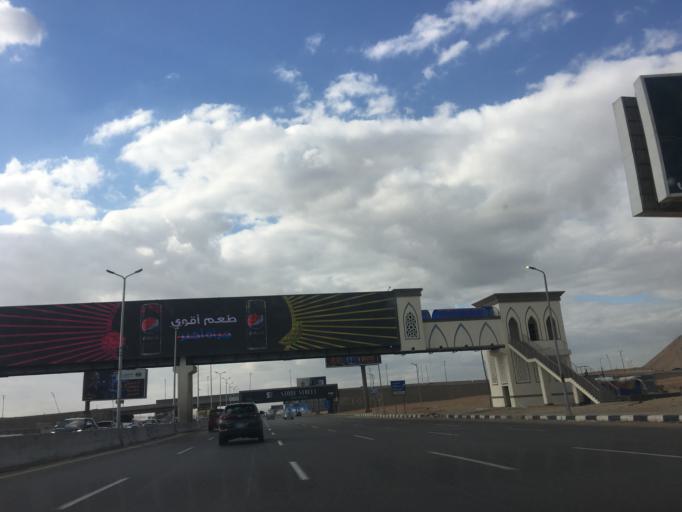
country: EG
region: Muhafazat al Qahirah
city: Cairo
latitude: 30.0221
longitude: 31.3723
